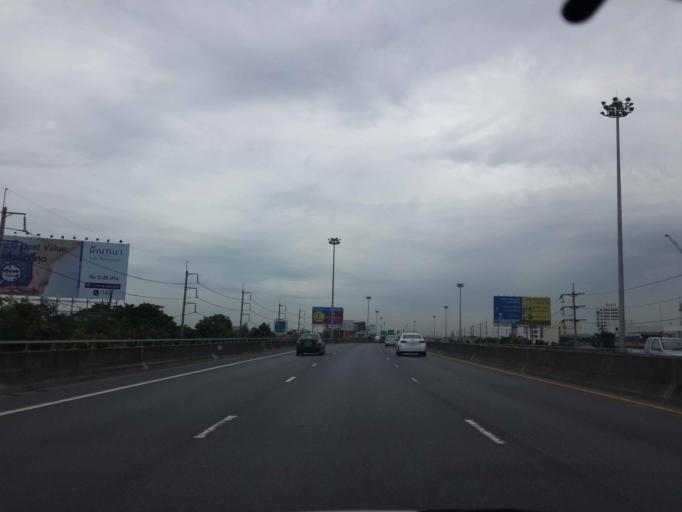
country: TH
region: Bangkok
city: Lat Phrao
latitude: 13.8334
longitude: 100.6308
